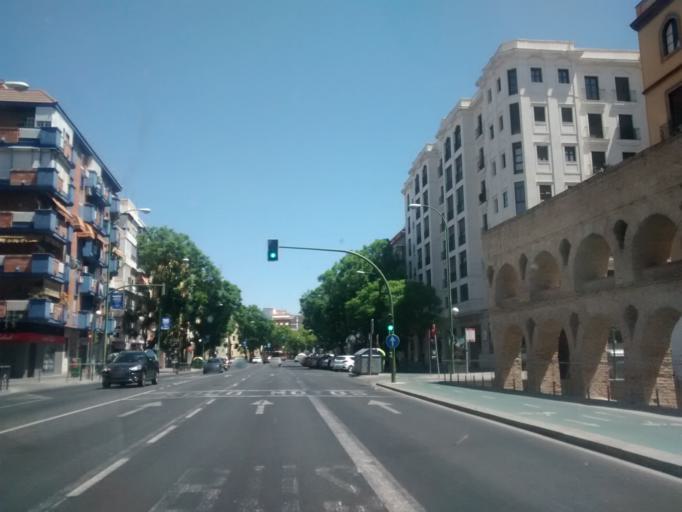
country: ES
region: Andalusia
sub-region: Provincia de Sevilla
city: Sevilla
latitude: 37.3878
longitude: -5.9815
